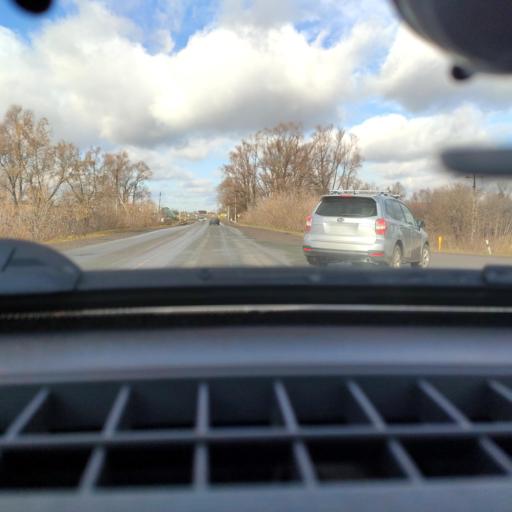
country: RU
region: Bashkortostan
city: Avdon
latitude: 54.7338
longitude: 55.8037
